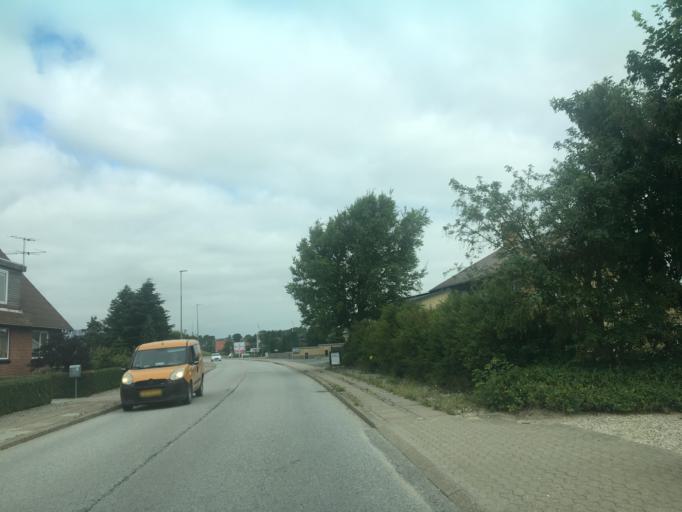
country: DK
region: North Denmark
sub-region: Thisted Kommune
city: Thisted
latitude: 56.8809
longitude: 8.6277
